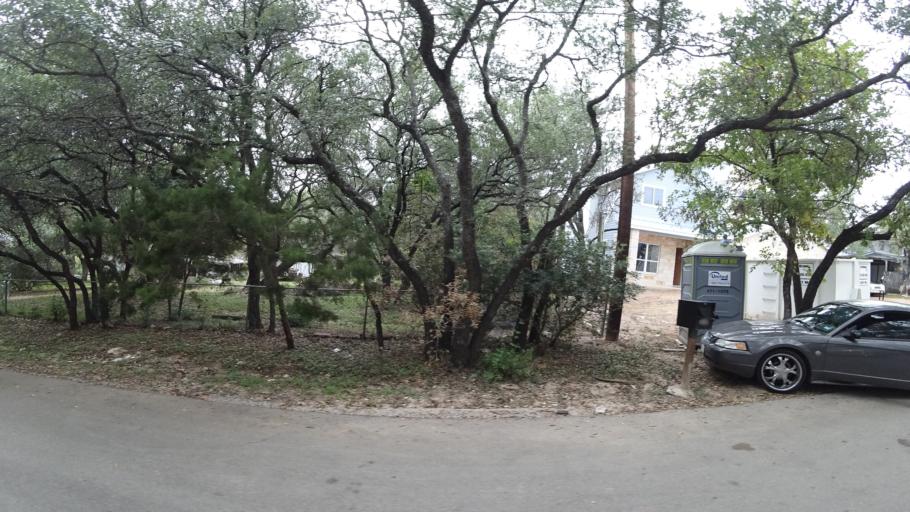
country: US
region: Texas
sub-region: Travis County
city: Bee Cave
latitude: 30.3317
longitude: -97.9288
